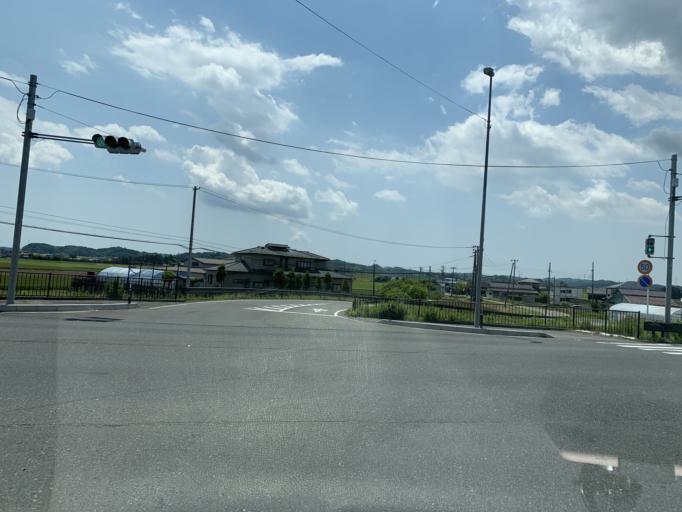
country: JP
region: Miyagi
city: Matsushima
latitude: 38.4547
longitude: 141.0865
